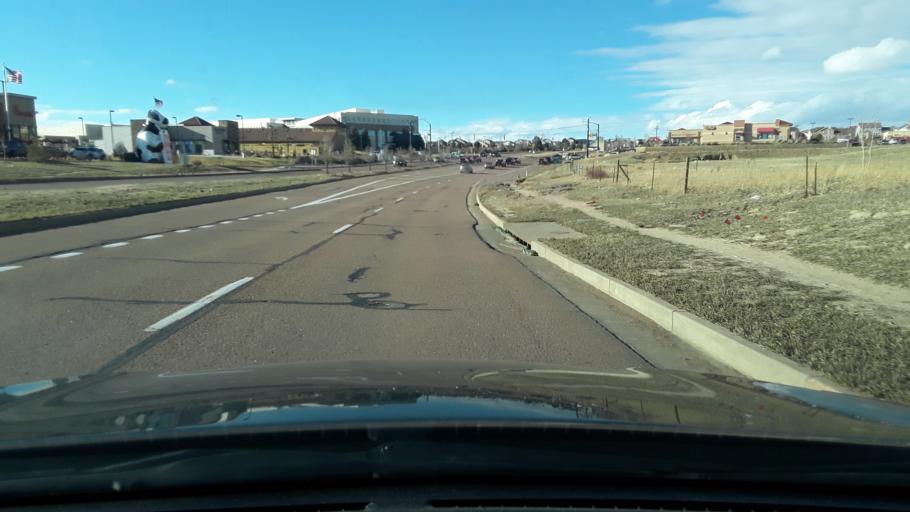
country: US
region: Colorado
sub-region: El Paso County
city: Gleneagle
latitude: 39.0231
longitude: -104.8163
